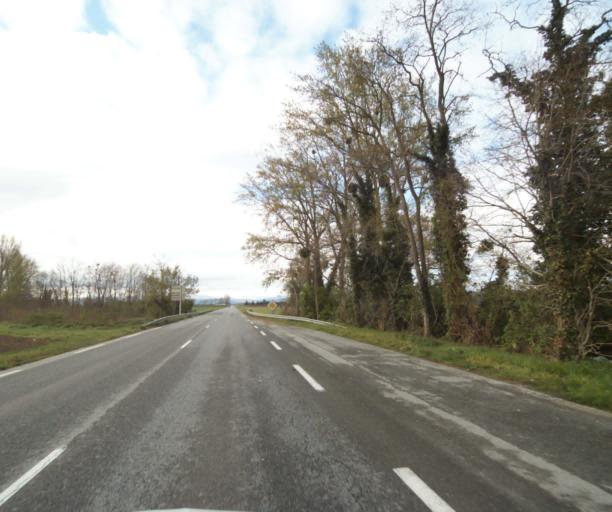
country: FR
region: Midi-Pyrenees
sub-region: Departement de l'Ariege
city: Saverdun
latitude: 43.2194
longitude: 1.6070
